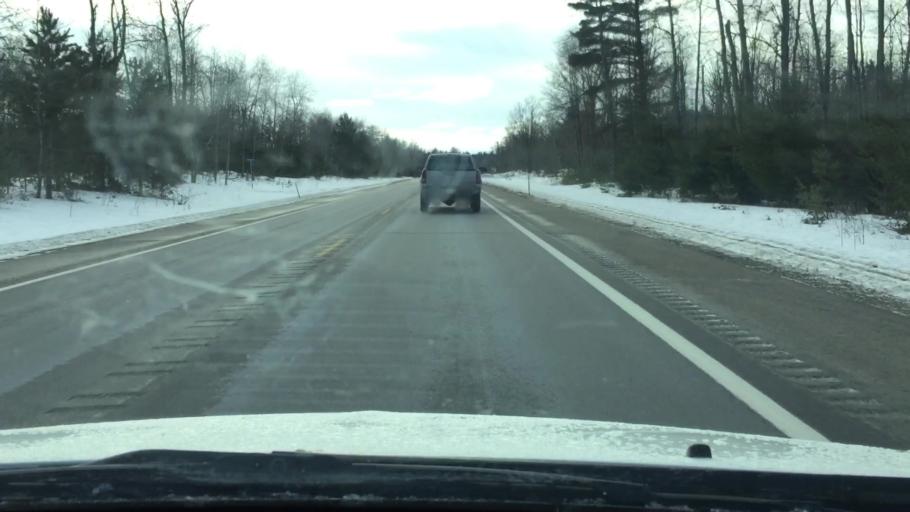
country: US
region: Michigan
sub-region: Kalkaska County
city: Kalkaska
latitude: 44.6563
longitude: -85.2589
